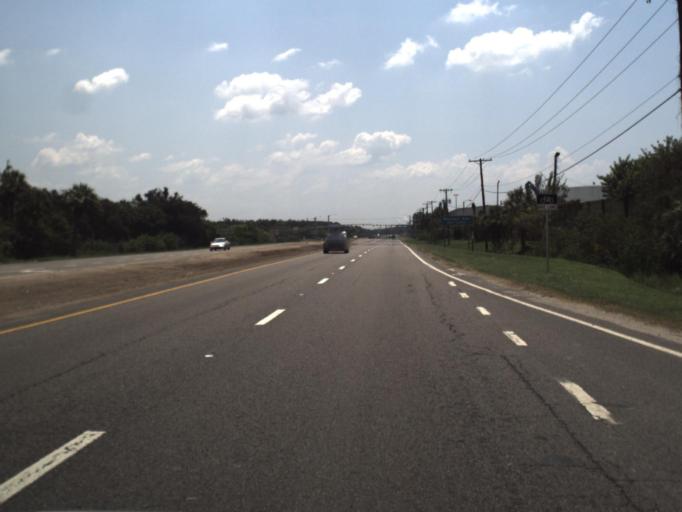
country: US
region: Florida
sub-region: Hillsborough County
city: Palm River-Clair Mel
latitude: 27.9057
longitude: -82.4020
